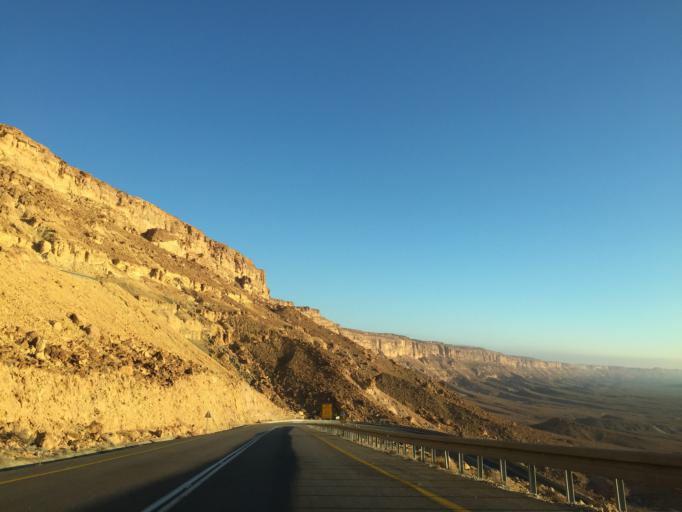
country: IL
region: Southern District
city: Mitzpe Ramon
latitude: 30.6217
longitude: 34.8179
